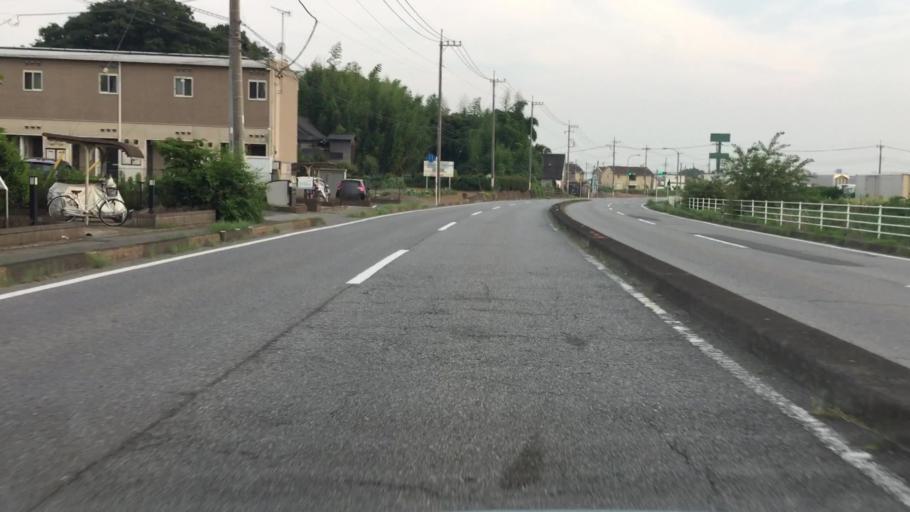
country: JP
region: Tochigi
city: Tochigi
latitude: 36.3343
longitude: 139.6946
